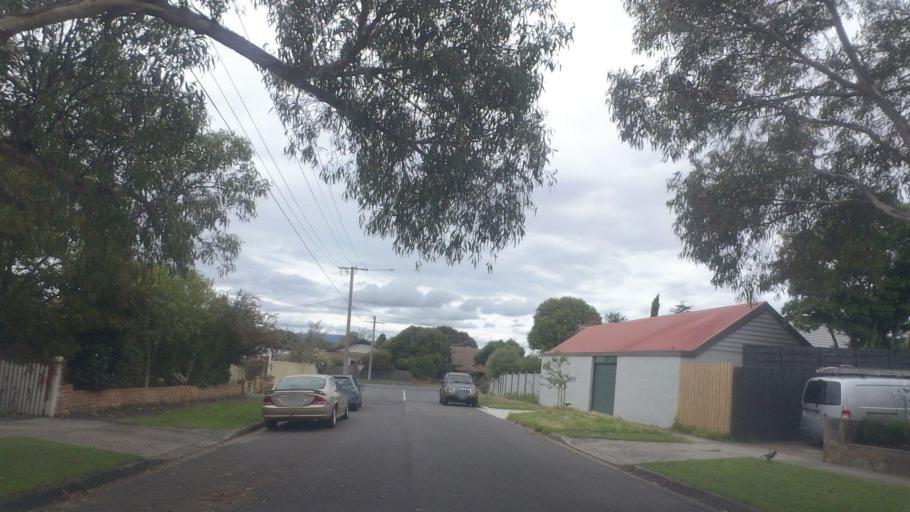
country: AU
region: Victoria
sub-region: Whitehorse
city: Box Hill South
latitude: -37.8306
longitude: 145.1207
